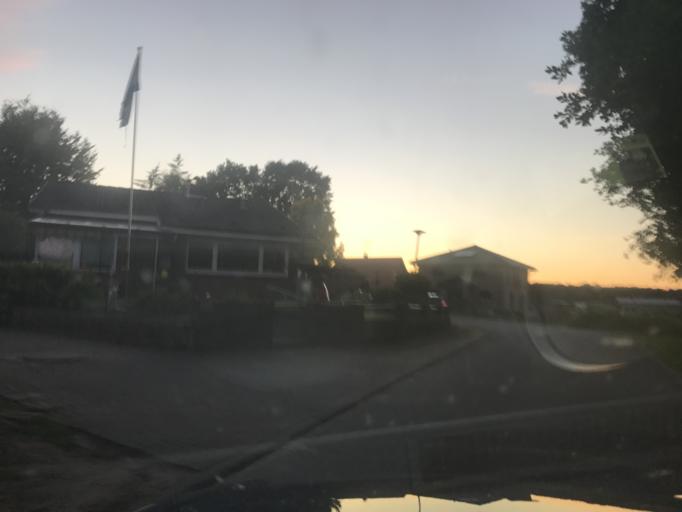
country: DE
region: Schleswig-Holstein
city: Burg
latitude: 54.0026
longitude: 9.2698
